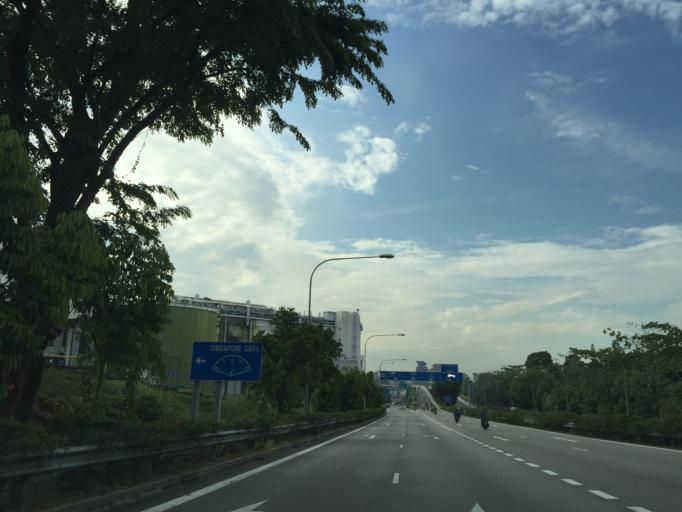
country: MY
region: Johor
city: Johor Bahru
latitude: 1.4355
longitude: 103.7685
